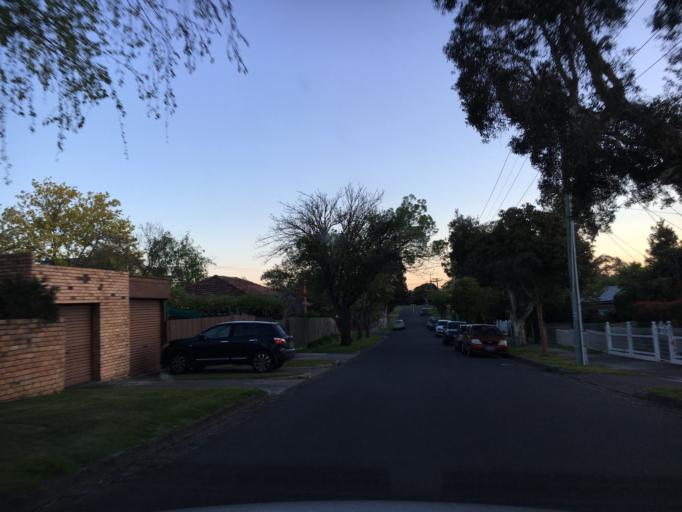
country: AU
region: Victoria
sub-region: Monash
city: Chadstone
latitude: -37.8979
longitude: 145.1040
